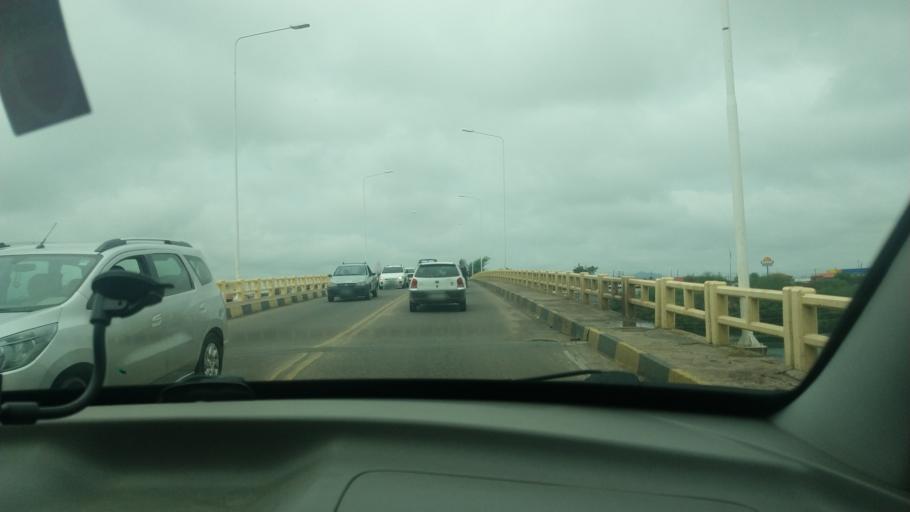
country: BR
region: Bahia
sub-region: Paulo Afonso
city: Paulo Afonso
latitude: -9.4005
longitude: -38.2339
